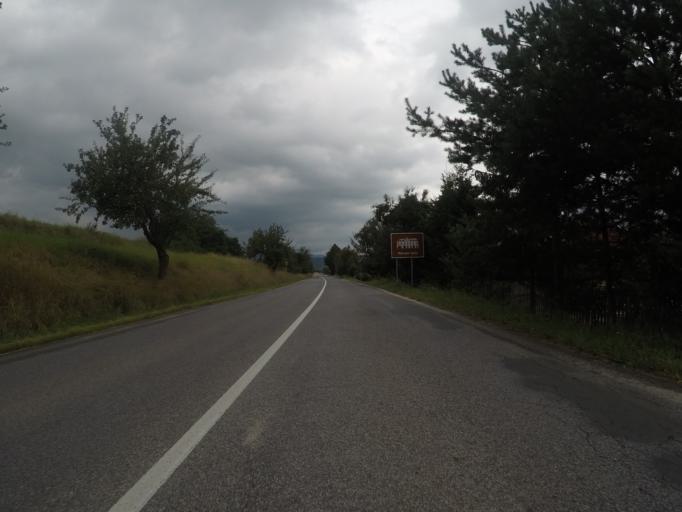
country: SK
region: Kosicky
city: Spisska Nova Ves
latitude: 48.9283
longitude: 20.5466
